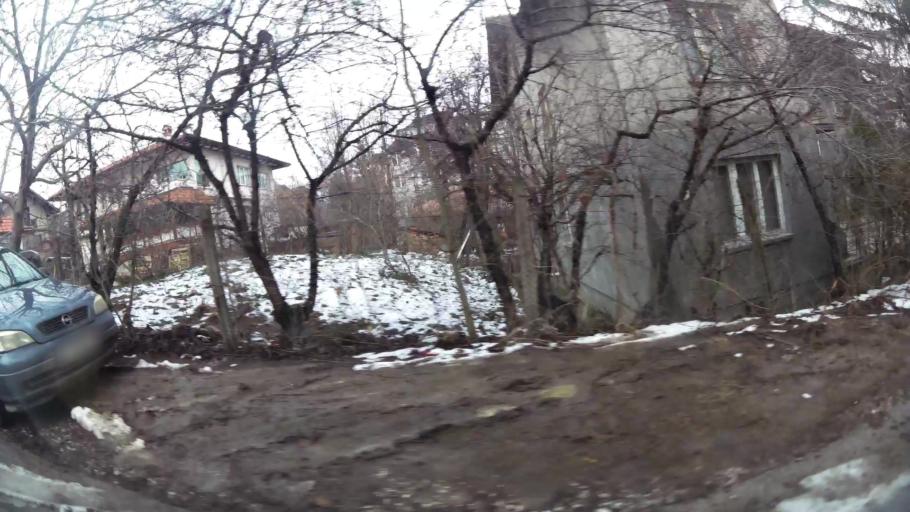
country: BG
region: Sofia-Capital
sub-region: Stolichna Obshtina
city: Sofia
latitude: 42.6646
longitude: 23.2424
